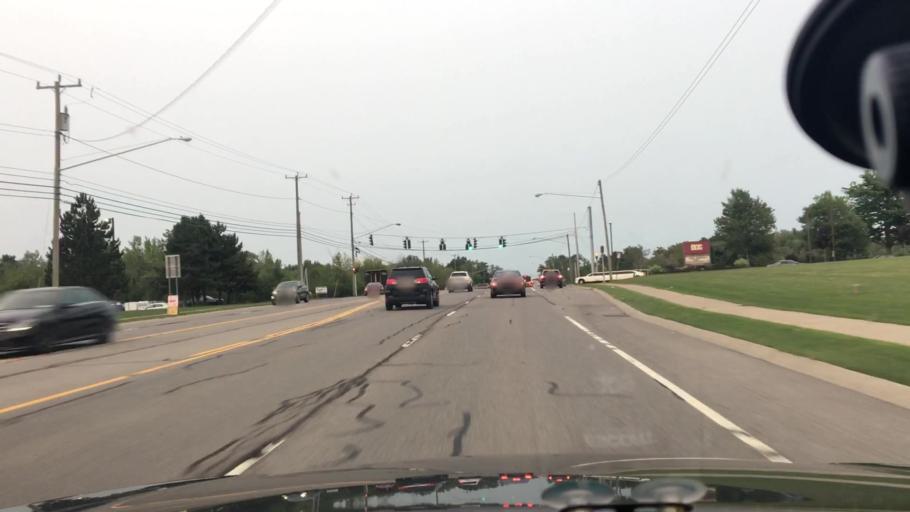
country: US
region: New York
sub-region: Erie County
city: Blasdell
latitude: 42.7737
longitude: -78.8017
